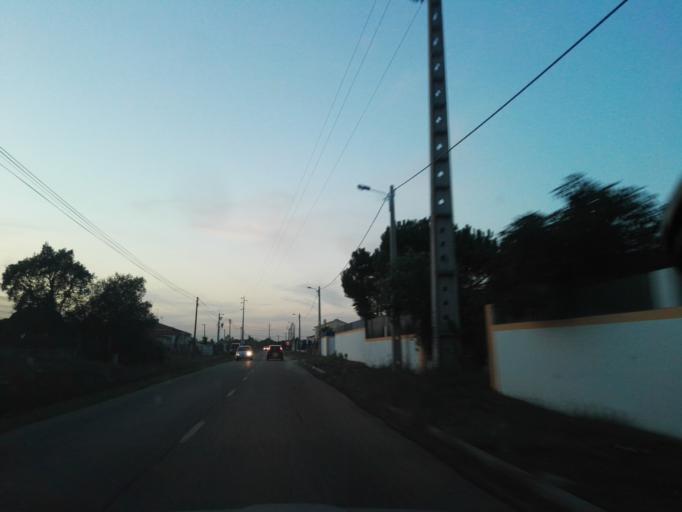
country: PT
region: Santarem
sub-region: Benavente
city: Benavente
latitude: 38.9407
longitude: -8.8001
